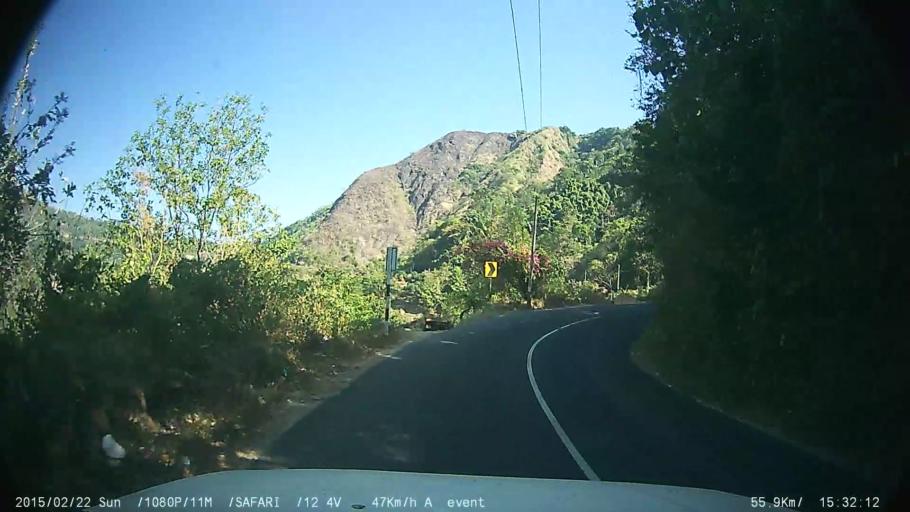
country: IN
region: Kerala
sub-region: Kottayam
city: Erattupetta
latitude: 9.5579
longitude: 76.9609
